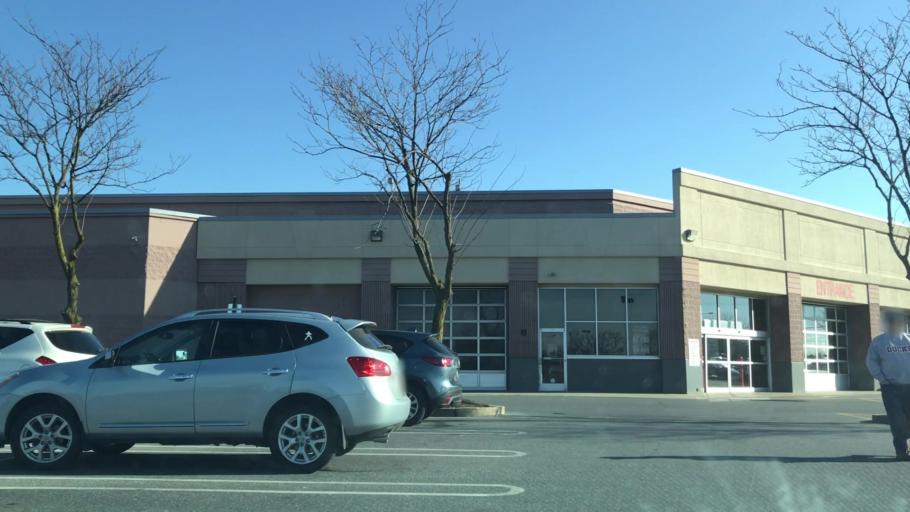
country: US
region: Pennsylvania
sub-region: Lancaster County
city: Lancaster
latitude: 40.0523
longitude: -76.2568
